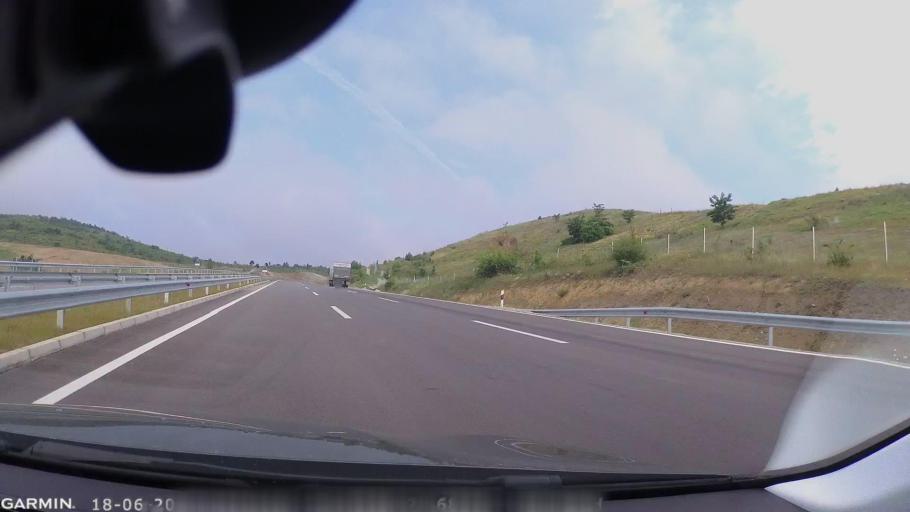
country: MK
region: Petrovec
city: Sredno Konjare
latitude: 41.9447
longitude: 21.7855
